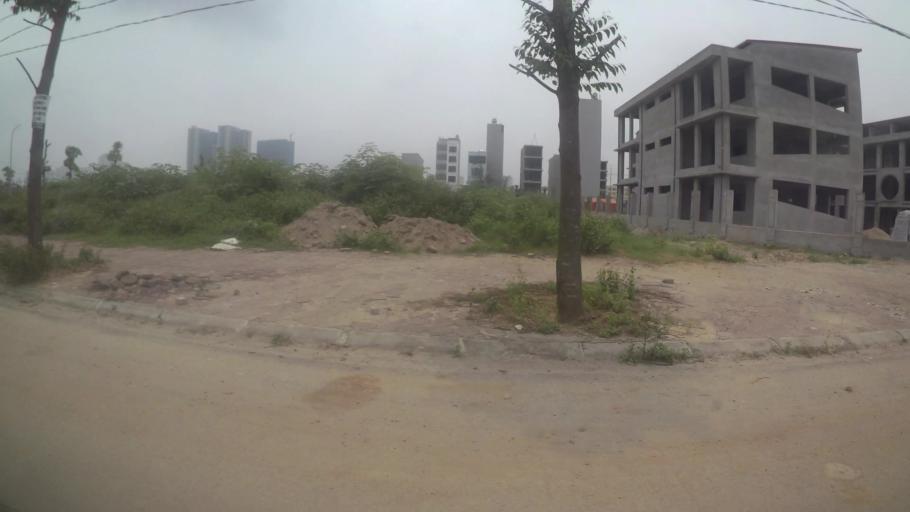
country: VN
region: Ha Noi
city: Ha Dong
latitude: 20.9782
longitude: 105.7684
